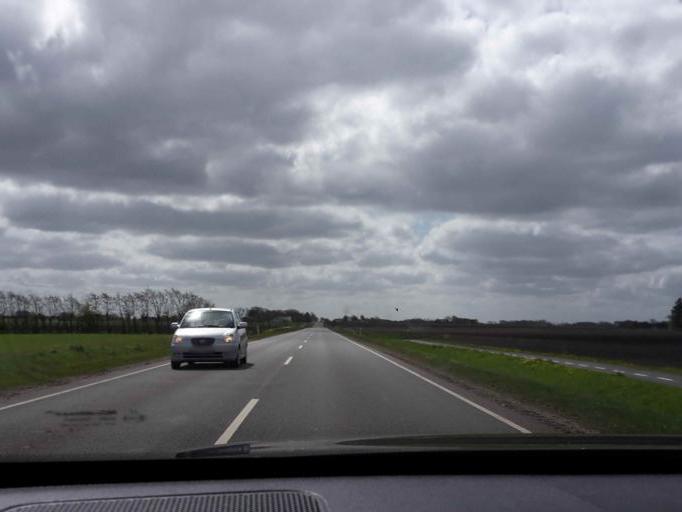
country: DK
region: South Denmark
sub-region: Varde Kommune
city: Olgod
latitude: 55.7576
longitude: 8.6200
